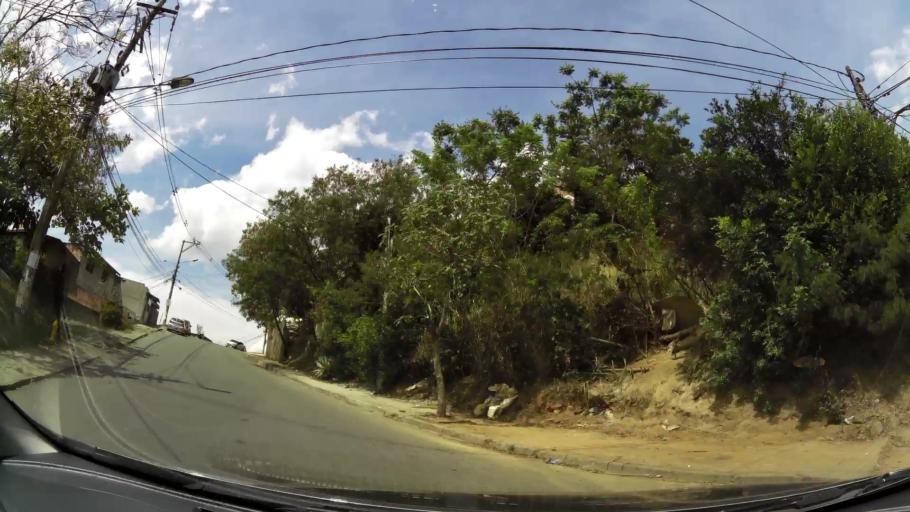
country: CO
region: Antioquia
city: Bello
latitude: 6.3479
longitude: -75.5496
